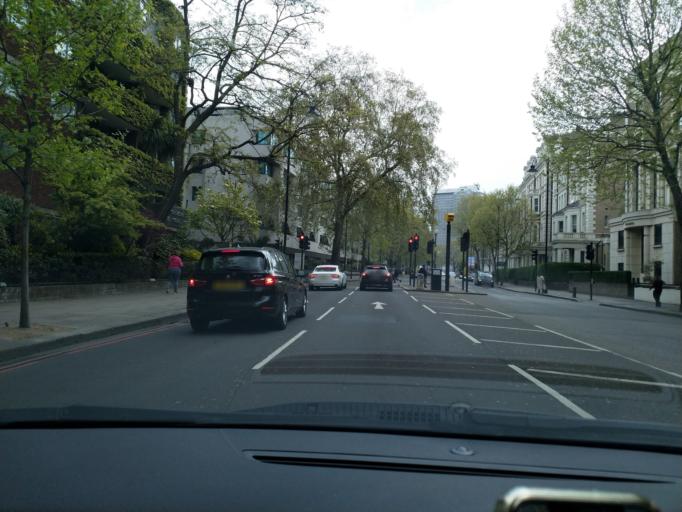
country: GB
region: England
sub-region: Greater London
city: Kensington
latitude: 51.4948
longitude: -0.1928
